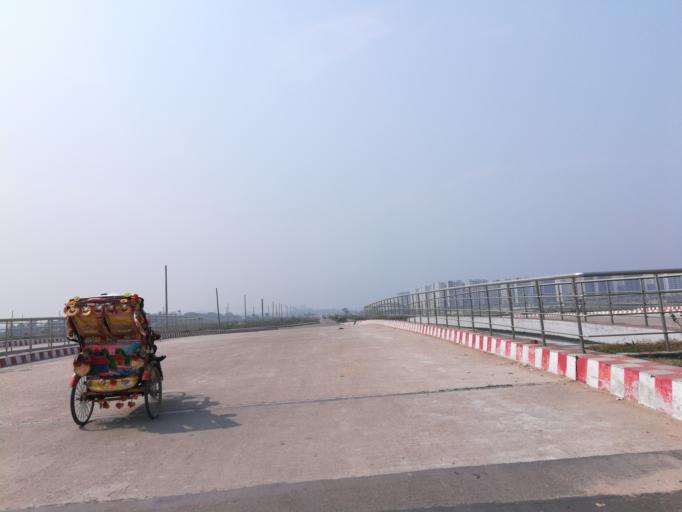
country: BD
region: Dhaka
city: Tungi
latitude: 23.8650
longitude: 90.3605
